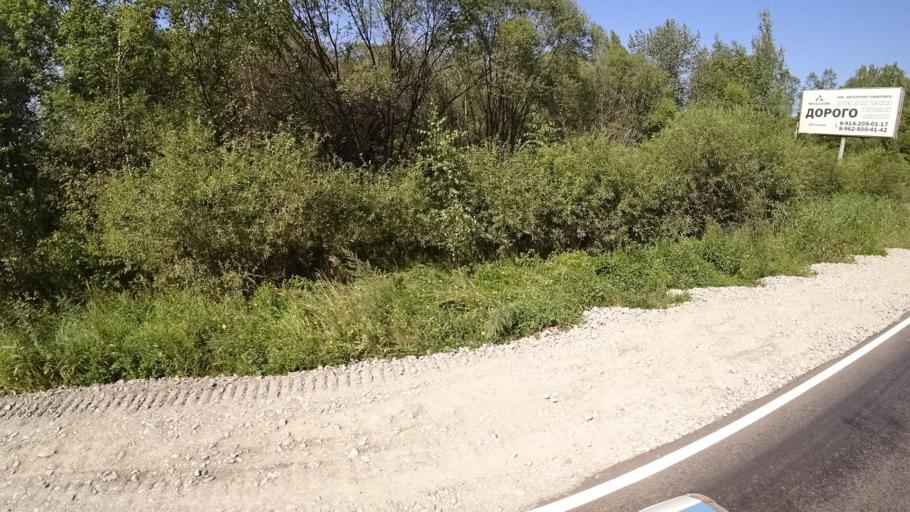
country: RU
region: Khabarovsk Krai
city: Khor
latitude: 47.9752
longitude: 135.0681
